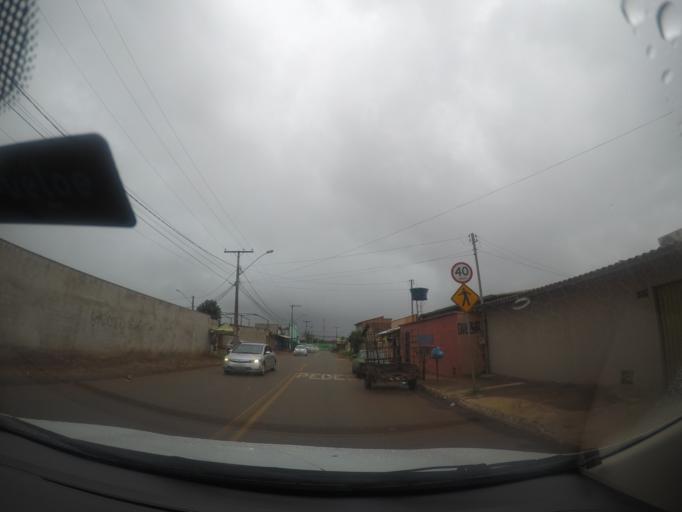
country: BR
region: Goias
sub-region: Goiania
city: Goiania
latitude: -16.6177
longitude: -49.3579
